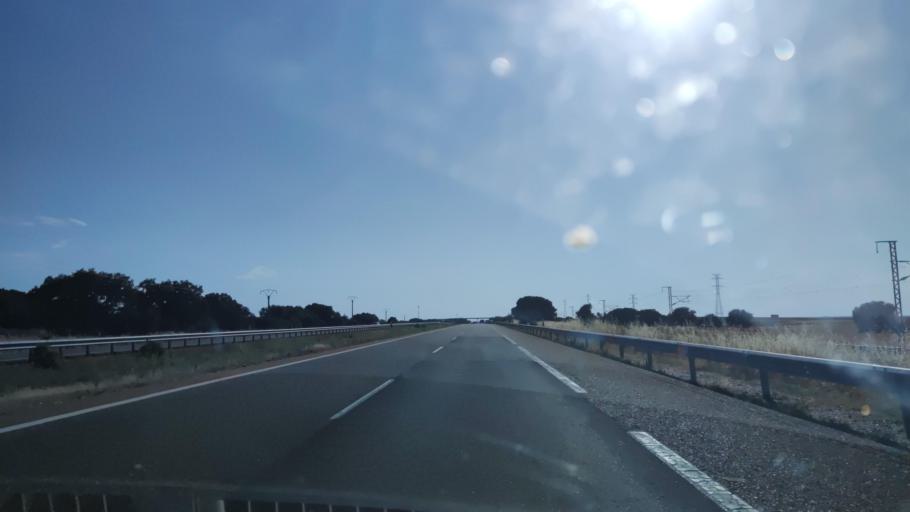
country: ES
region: Castille and Leon
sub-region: Provincia de Salamanca
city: Galindo y Perahuy
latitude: 40.9260
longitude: -5.8337
